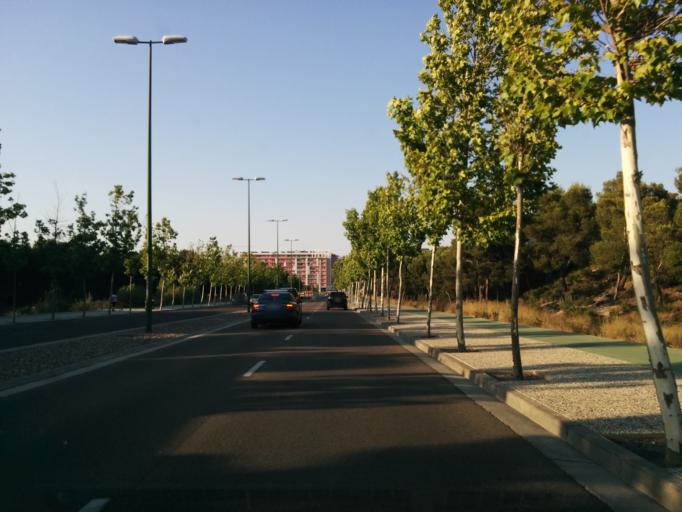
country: ES
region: Aragon
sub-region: Provincia de Zaragoza
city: Zaragoza
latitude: 41.6115
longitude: -0.8768
